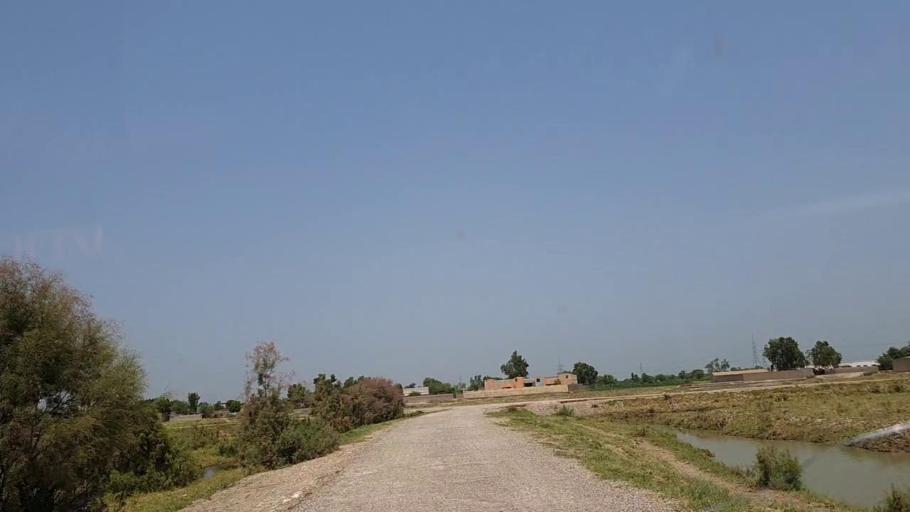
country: PK
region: Sindh
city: Ghotki
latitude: 27.9907
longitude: 69.3694
